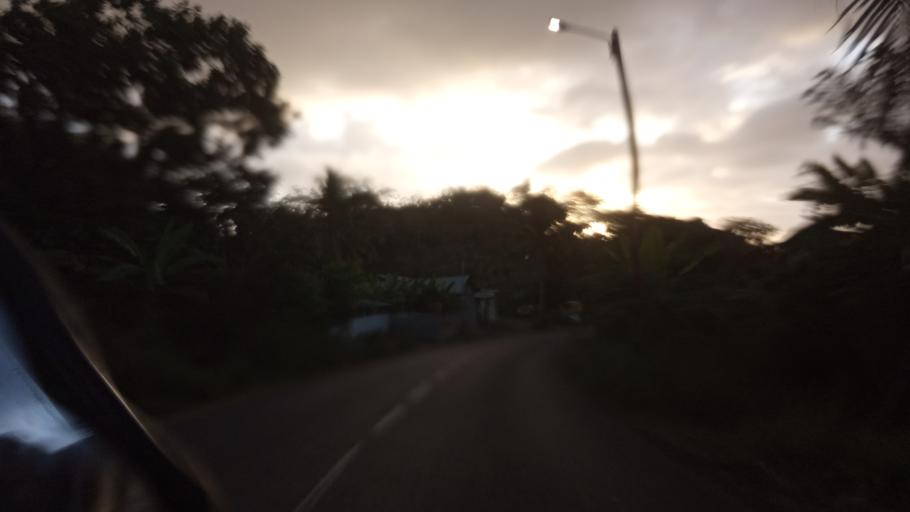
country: YT
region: Kani-Keli
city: Kani Keli
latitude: -12.9263
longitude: 45.1080
